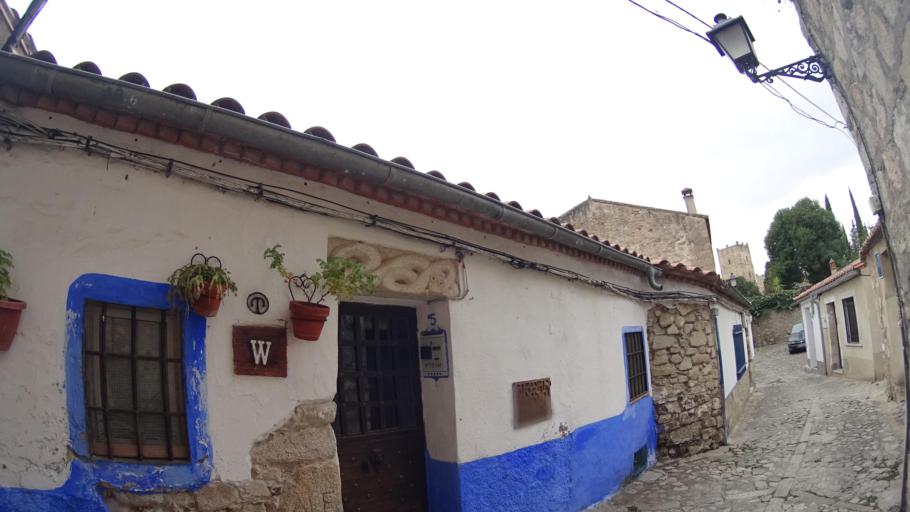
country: ES
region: Extremadura
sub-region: Provincia de Caceres
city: Trujillo
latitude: 39.4600
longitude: -5.8848
